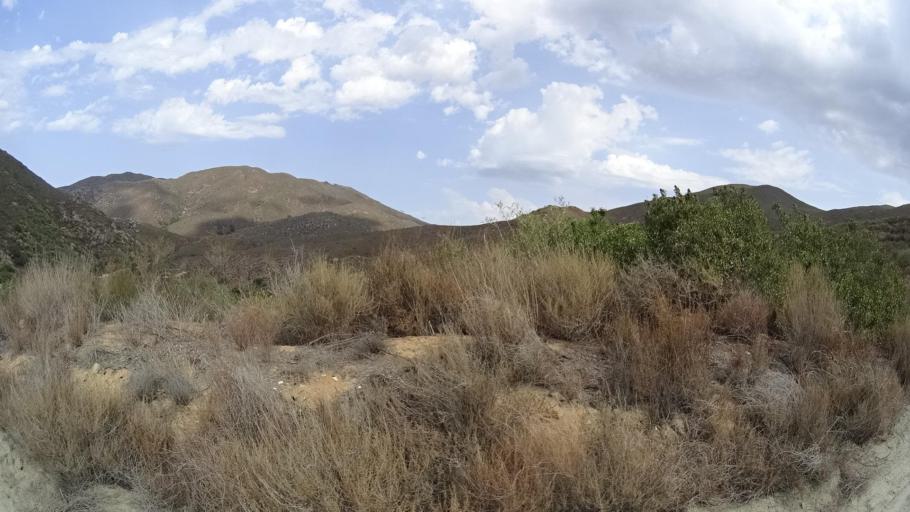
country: US
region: California
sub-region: San Diego County
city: Ramona
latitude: 33.1198
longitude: -116.7896
